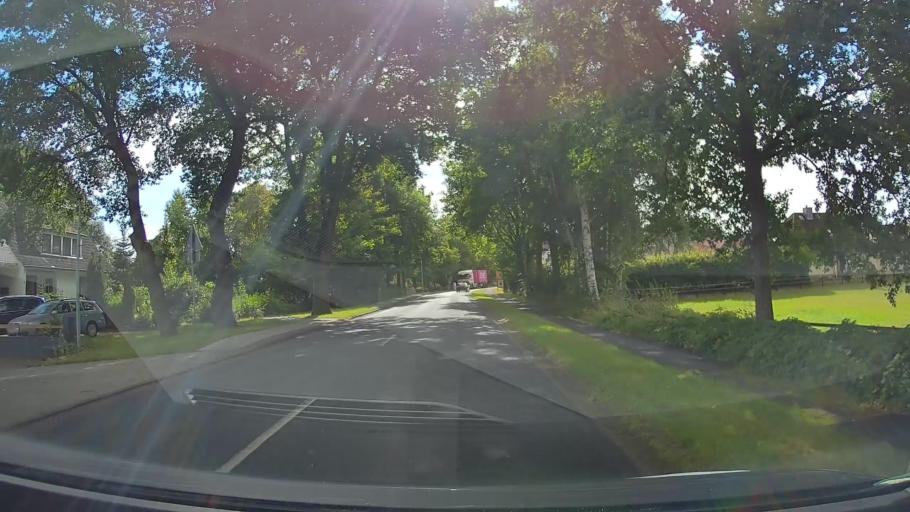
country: DE
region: Lower Saxony
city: Rhade
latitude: 53.3299
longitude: 9.1143
